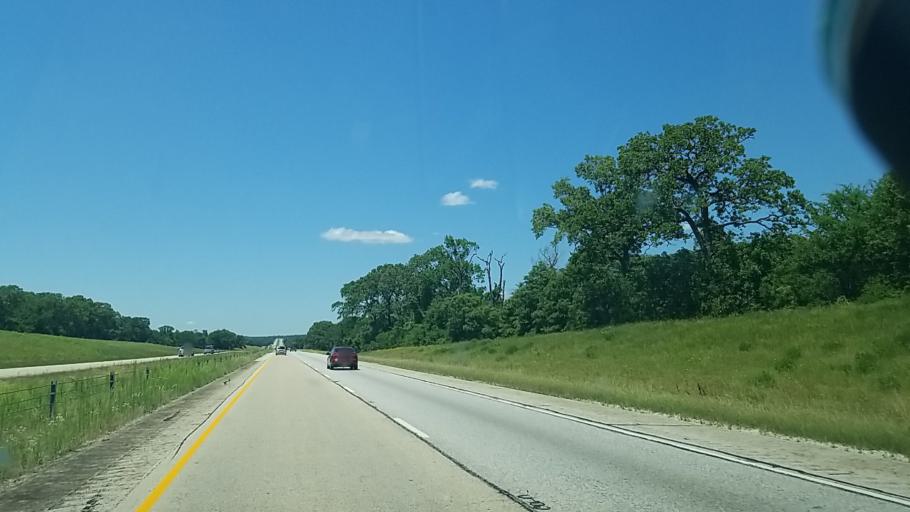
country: US
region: Texas
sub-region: Leon County
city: Centerville
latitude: 31.1676
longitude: -95.9871
